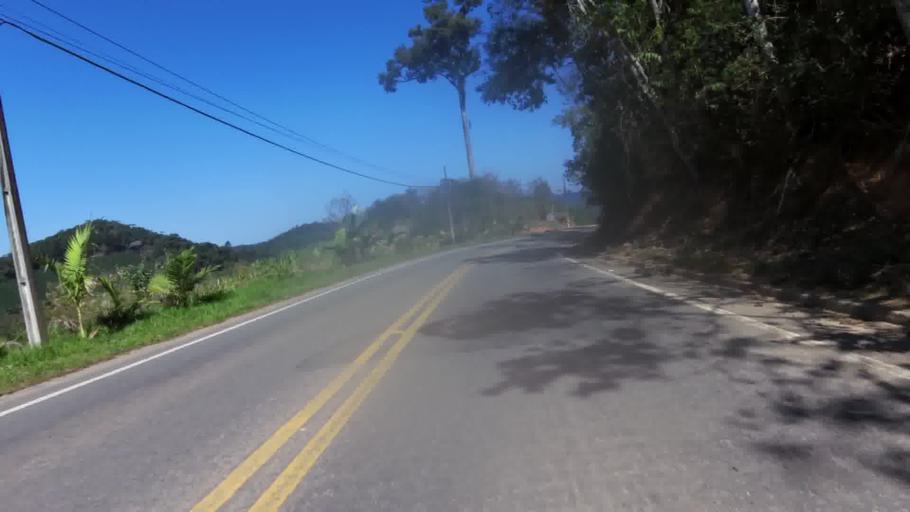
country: BR
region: Espirito Santo
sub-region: Marechal Floriano
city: Marechal Floriano
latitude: -20.4377
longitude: -40.7722
